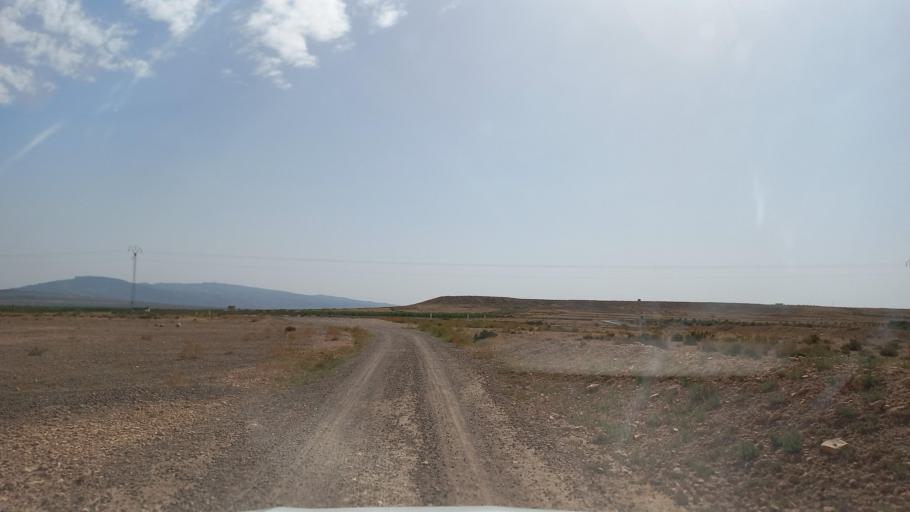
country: TN
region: Al Qasrayn
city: Kasserine
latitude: 35.2741
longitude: 8.9676
